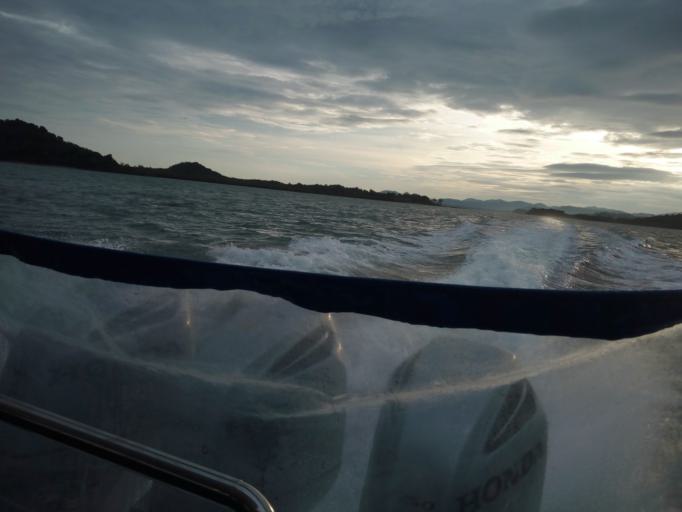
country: TH
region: Phangnga
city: Ko Yao
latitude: 8.0703
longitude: 98.4662
